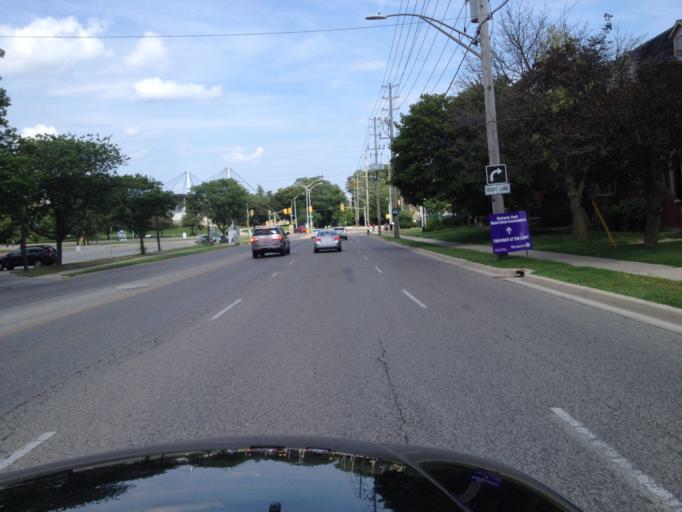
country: CA
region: Ontario
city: London
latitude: 43.0014
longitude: -81.2784
